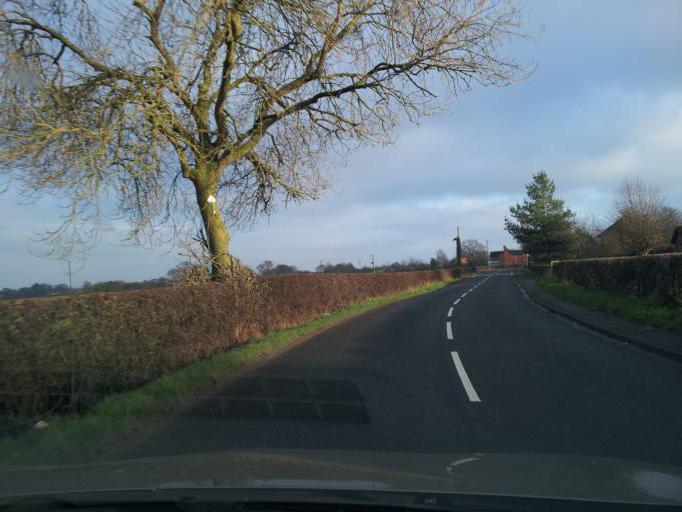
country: GB
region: England
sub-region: Staffordshire
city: Burton upon Trent
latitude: 52.8674
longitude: -1.6961
